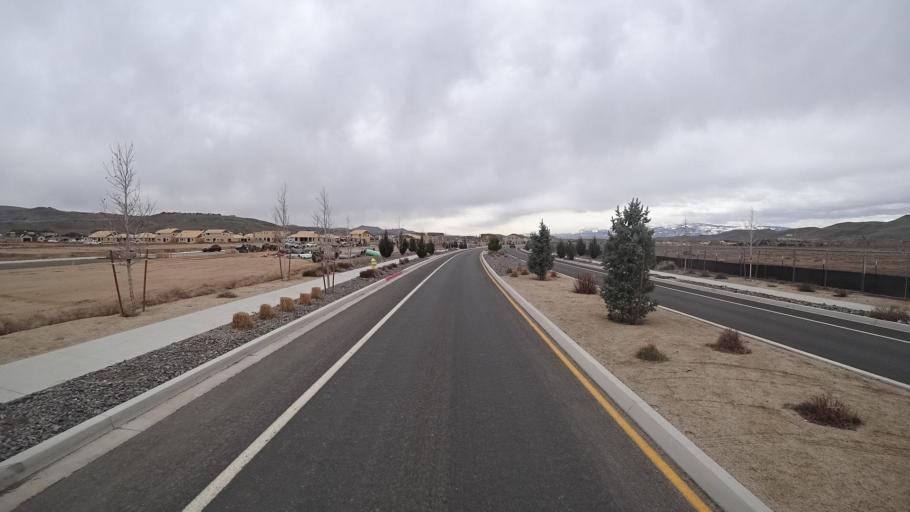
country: US
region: Nevada
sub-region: Washoe County
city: Spanish Springs
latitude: 39.6074
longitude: -119.7201
